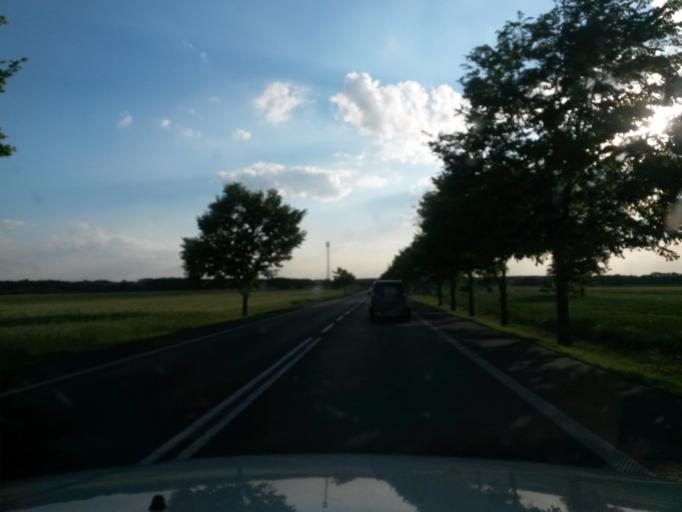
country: PL
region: Lodz Voivodeship
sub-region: Powiat belchatowski
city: Rusiec
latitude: 51.3127
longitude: 18.9057
